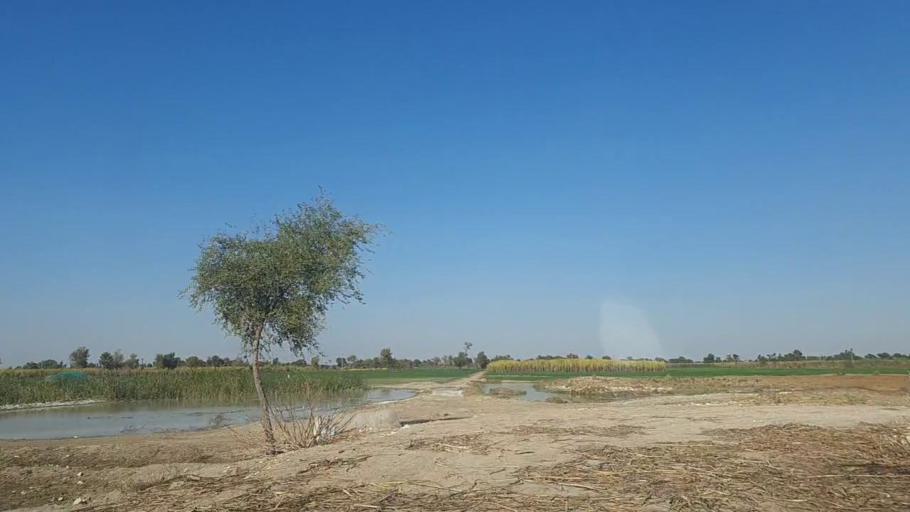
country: PK
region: Sindh
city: Sanghar
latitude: 26.2260
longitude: 68.9648
